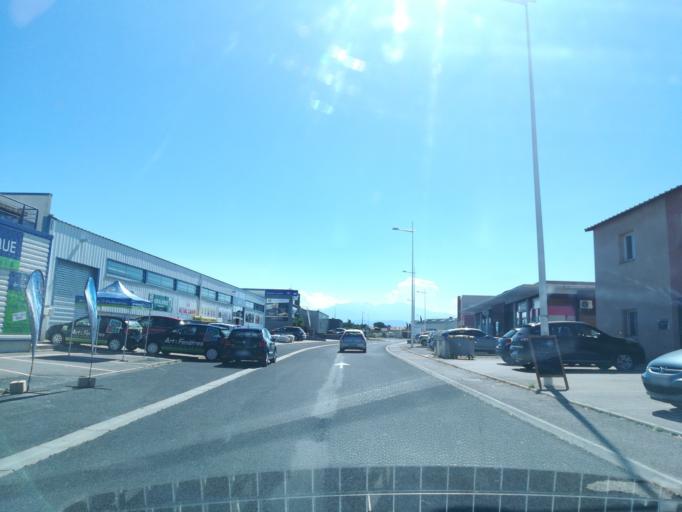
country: FR
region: Languedoc-Roussillon
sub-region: Departement des Pyrenees-Orientales
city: Pollestres
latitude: 42.6420
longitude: 2.8791
